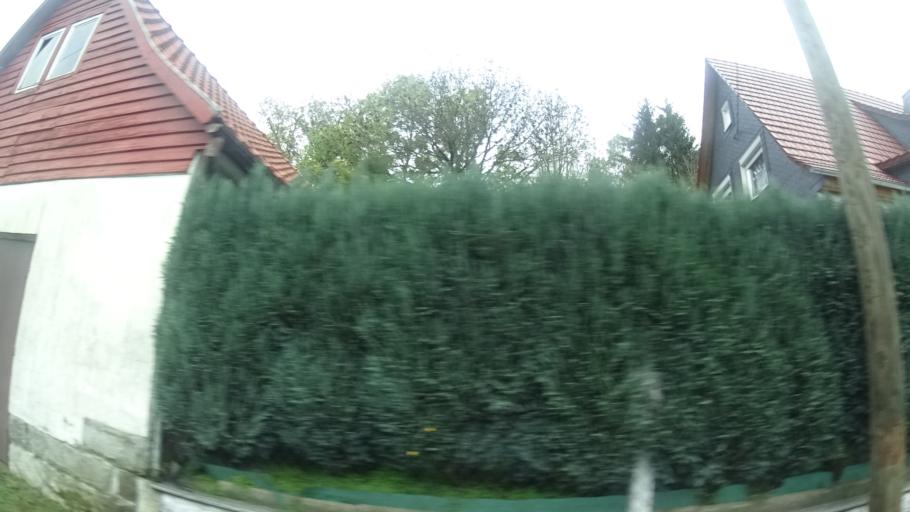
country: DE
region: Thuringia
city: Eisfeld
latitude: 50.4868
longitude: 10.8523
